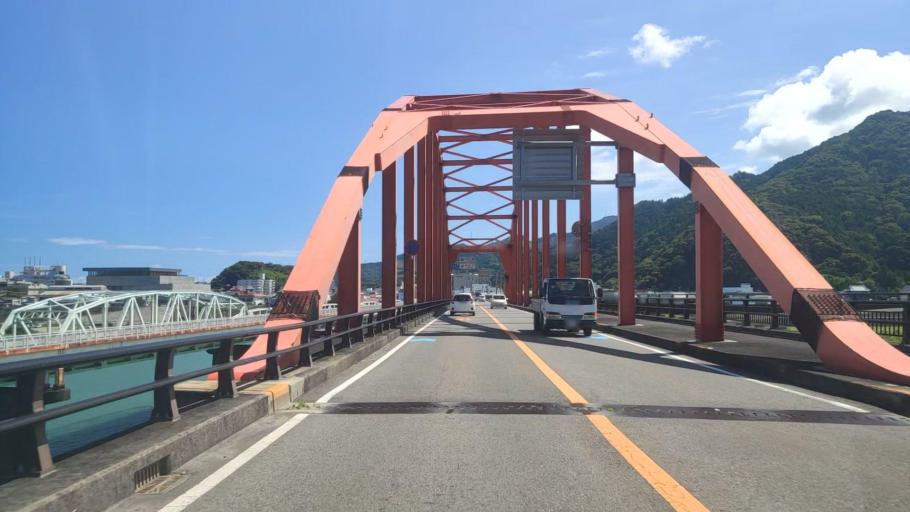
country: JP
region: Wakayama
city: Shingu
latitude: 33.7344
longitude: 135.9880
